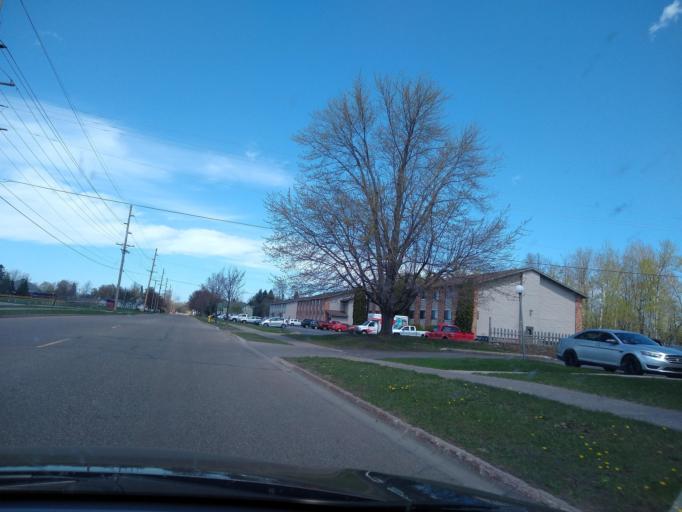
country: US
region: Michigan
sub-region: Marquette County
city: Marquette
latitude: 46.5656
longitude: -87.3961
